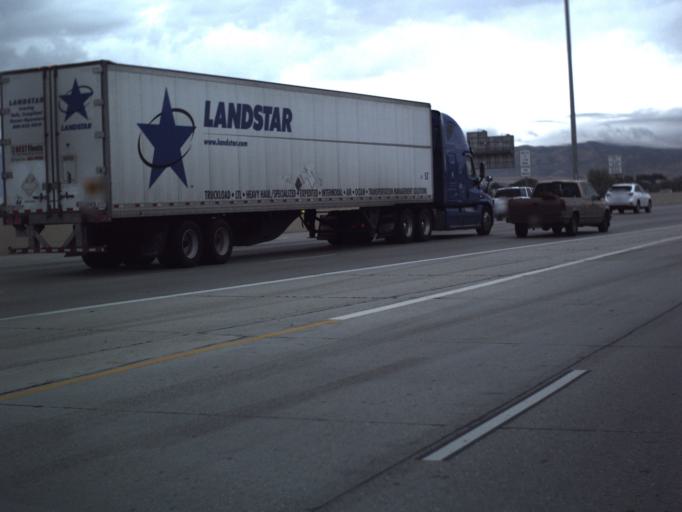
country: US
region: Utah
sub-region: Utah County
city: American Fork
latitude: 40.3786
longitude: -111.8211
